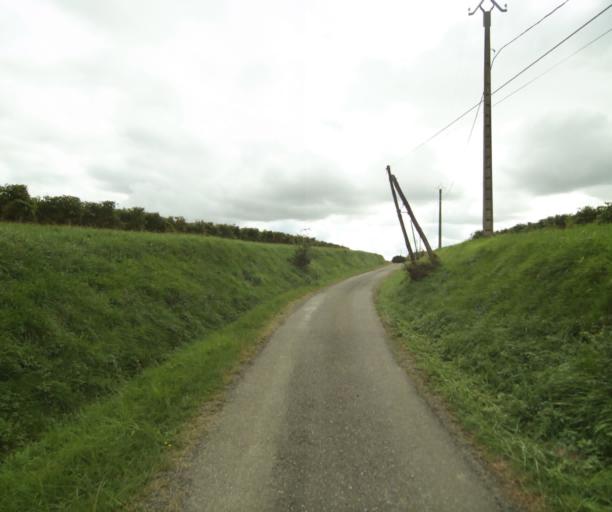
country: FR
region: Midi-Pyrenees
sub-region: Departement du Gers
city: Nogaro
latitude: 43.8325
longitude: -0.0069
